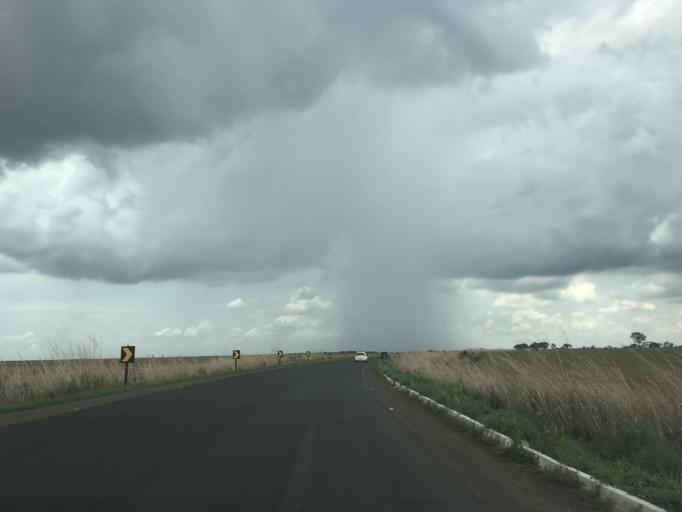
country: BR
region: Goias
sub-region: Vianopolis
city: Vianopolis
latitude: -16.8583
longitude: -48.5406
